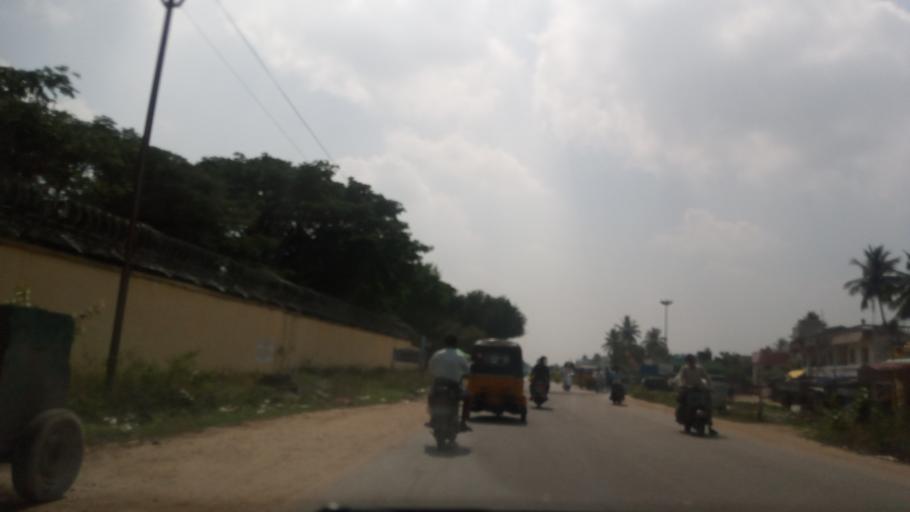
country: IN
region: Tamil Nadu
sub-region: Vellore
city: Arakkonam
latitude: 13.0680
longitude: 79.6730
